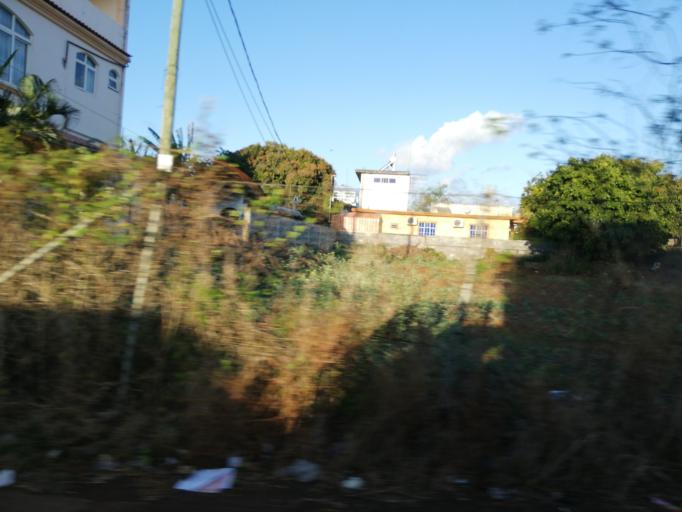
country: MU
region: Pamplemousses
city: Terre Rouge
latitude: -20.1226
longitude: 57.5315
